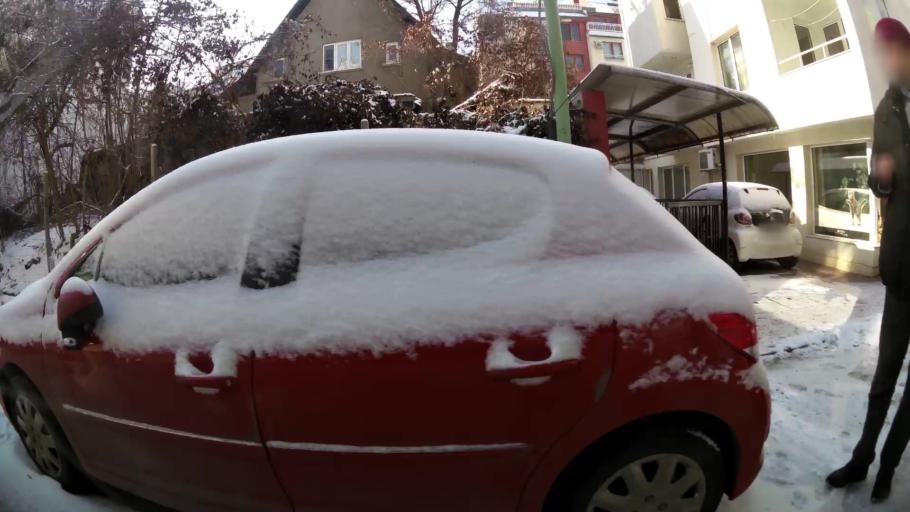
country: BG
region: Sofia-Capital
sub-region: Stolichna Obshtina
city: Sofia
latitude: 42.6813
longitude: 23.3252
